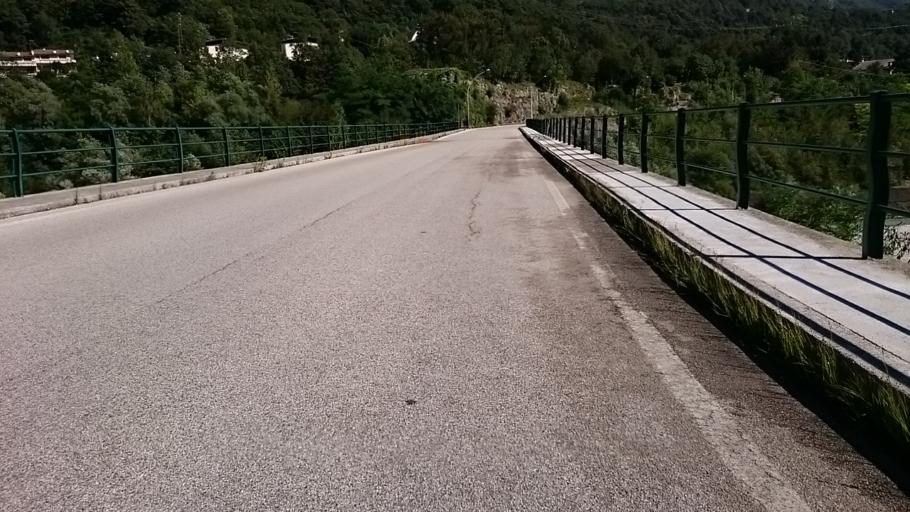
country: IT
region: Veneto
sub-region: Provincia di Belluno
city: Castello Lavazzo
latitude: 46.2808
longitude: 12.3082
